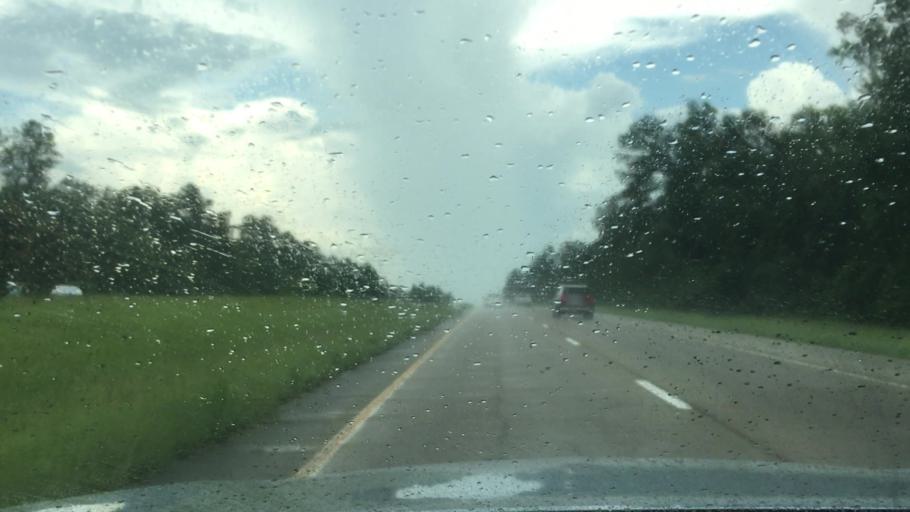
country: US
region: Mississippi
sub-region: Lamar County
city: Purvis
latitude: 31.1553
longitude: -89.3597
